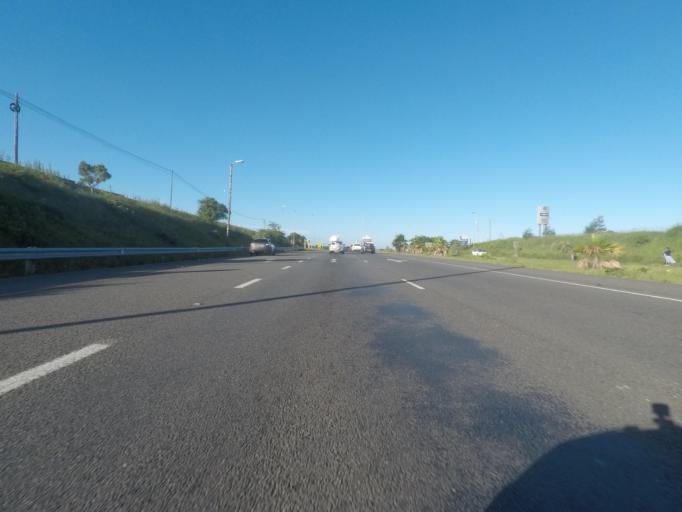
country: ZA
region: Eastern Cape
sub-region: Buffalo City Metropolitan Municipality
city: East London
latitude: -33.0393
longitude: 27.8317
